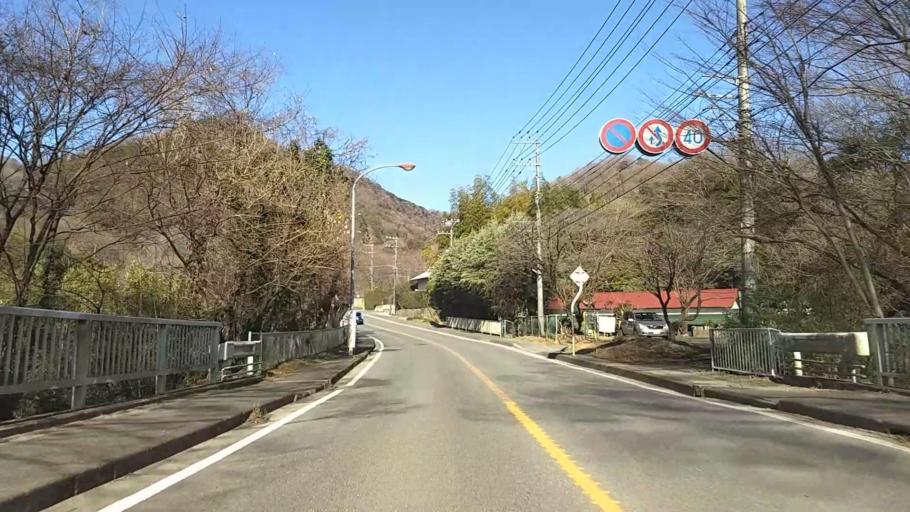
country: JP
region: Kanagawa
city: Atsugi
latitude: 35.4818
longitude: 139.3038
